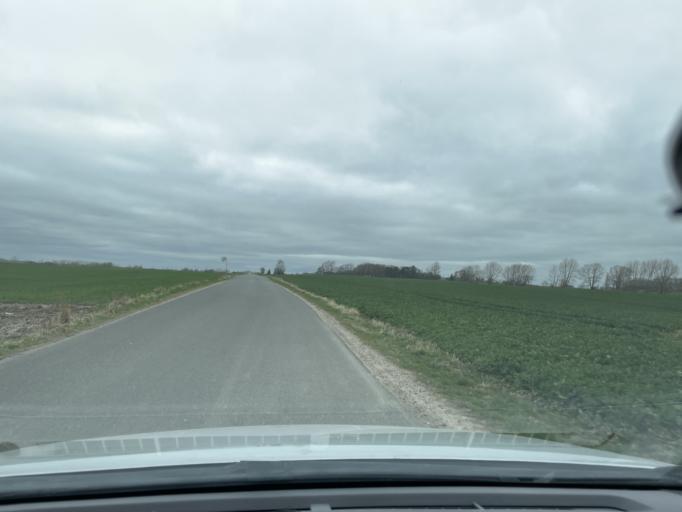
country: DK
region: South Denmark
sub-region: Nyborg Kommune
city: Nyborg
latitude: 55.3540
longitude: 10.7441
